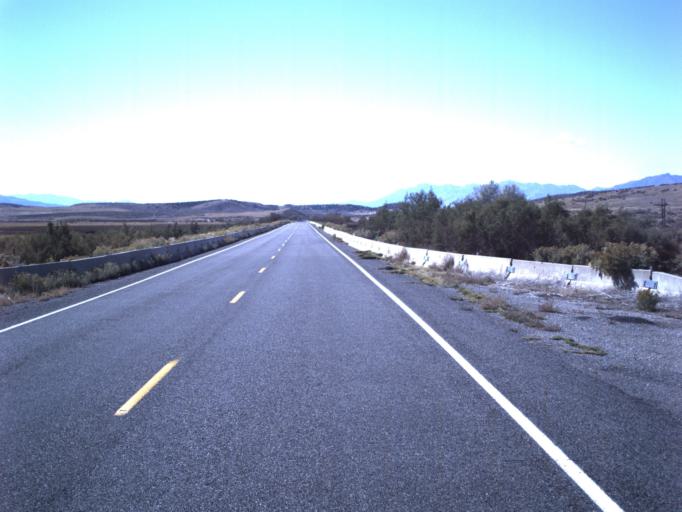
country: US
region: Utah
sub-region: Juab County
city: Nephi
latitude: 39.4976
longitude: -111.9610
